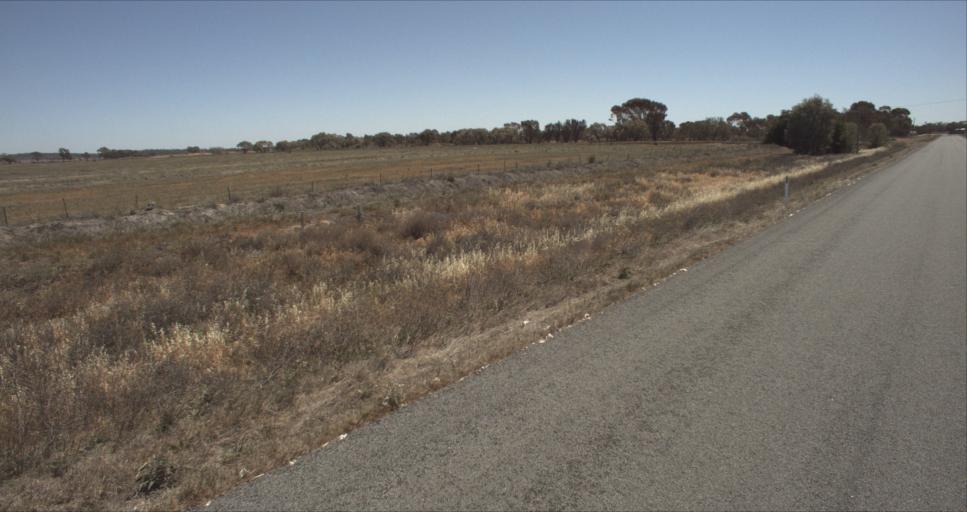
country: AU
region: New South Wales
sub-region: Leeton
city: Leeton
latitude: -34.4324
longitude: 146.2994
